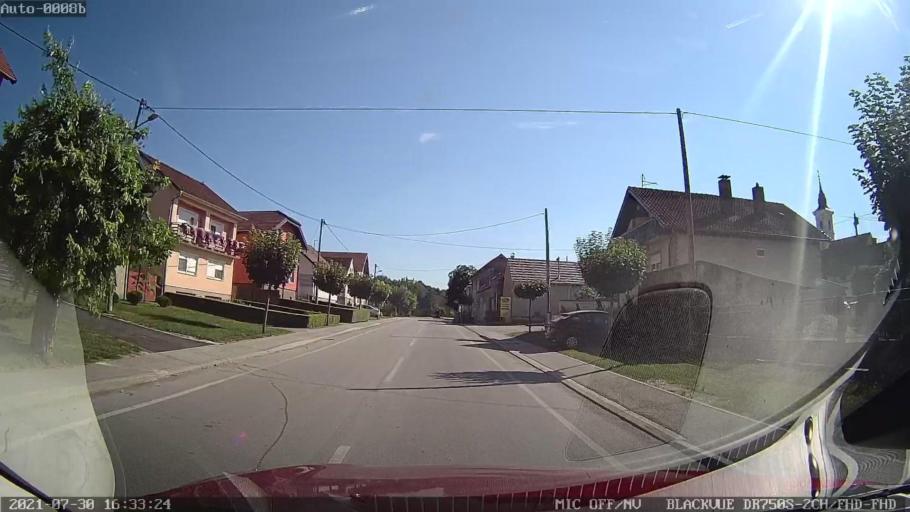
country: HR
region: Varazdinska
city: Jalzabet
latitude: 46.2586
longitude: 16.4740
